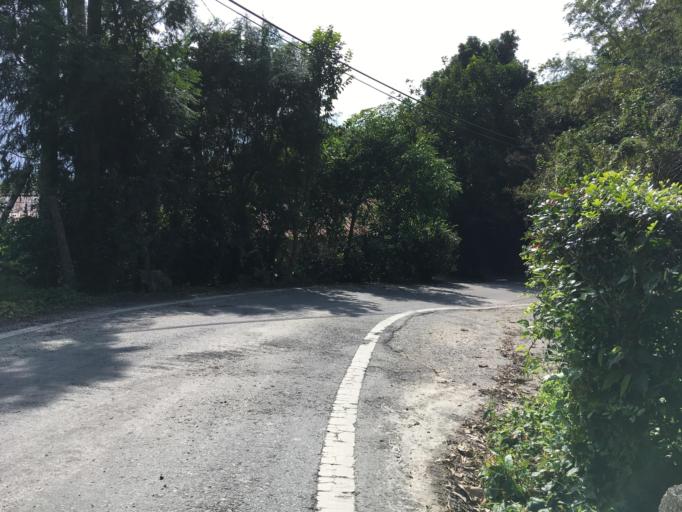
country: TW
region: Taiwan
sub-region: Yilan
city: Yilan
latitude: 24.8410
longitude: 121.7808
